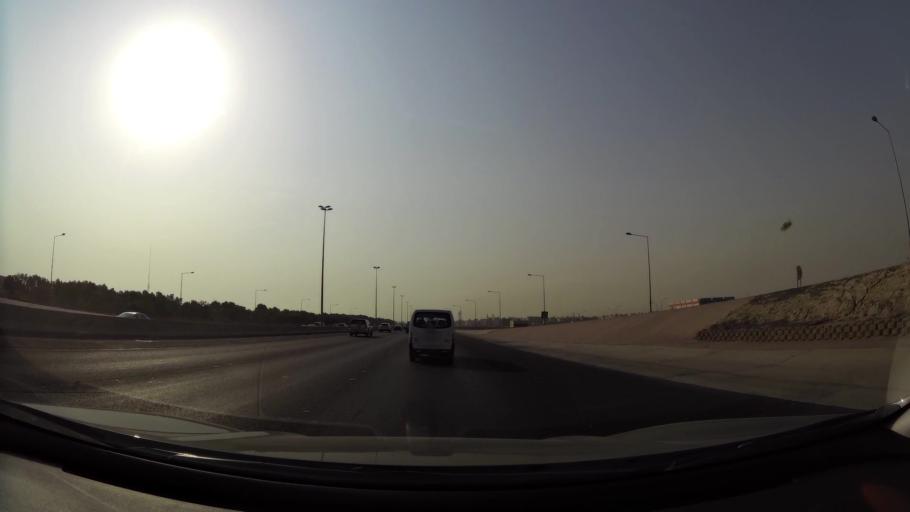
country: KW
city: Al Funaytis
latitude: 29.2474
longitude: 48.0921
